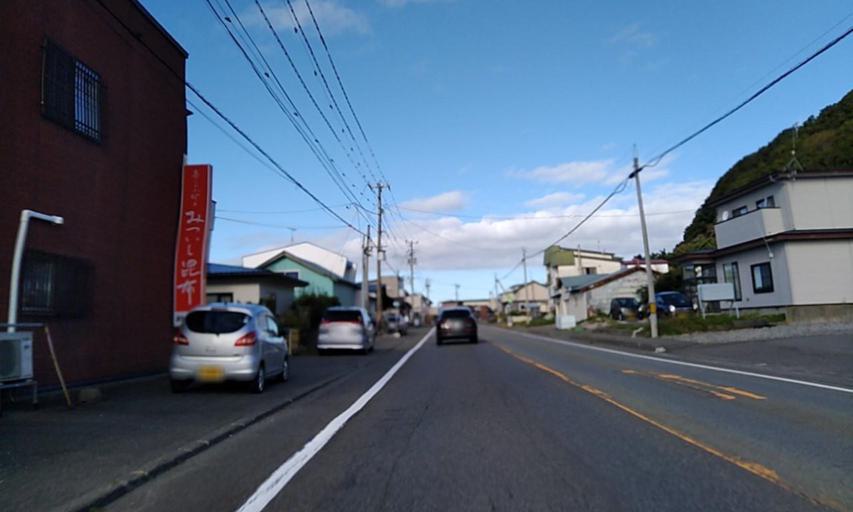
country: JP
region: Hokkaido
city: Shizunai-furukawacho
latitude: 42.2512
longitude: 142.5461
